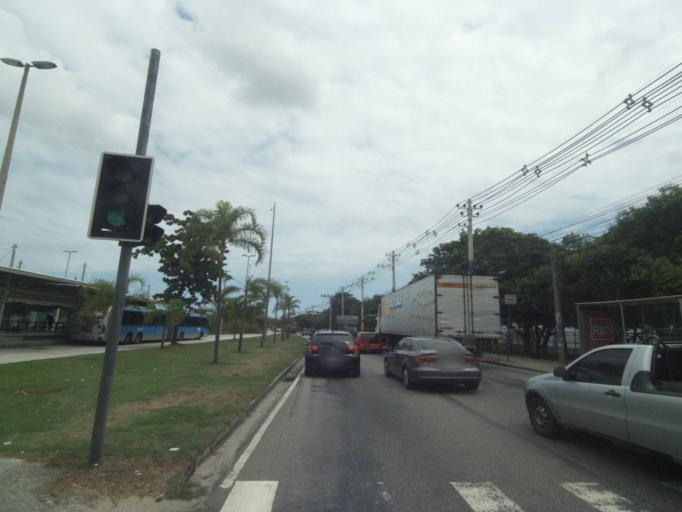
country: BR
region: Rio de Janeiro
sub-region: Sao Joao De Meriti
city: Sao Joao de Meriti
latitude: -22.9405
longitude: -43.3728
